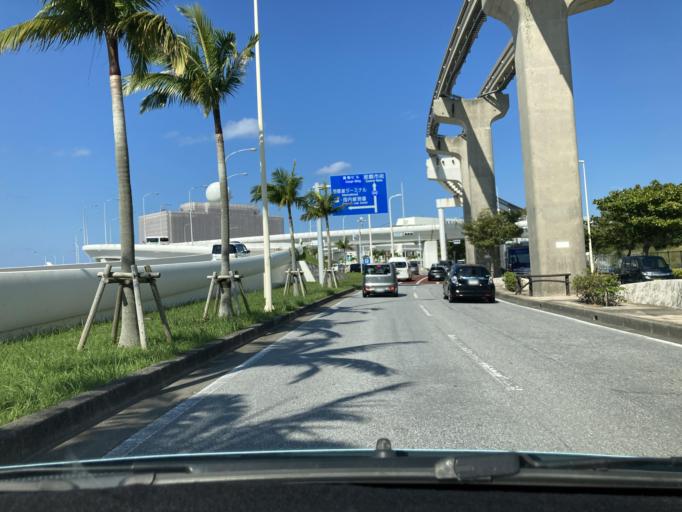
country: JP
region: Okinawa
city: Naha-shi
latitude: 26.2029
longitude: 127.6533
